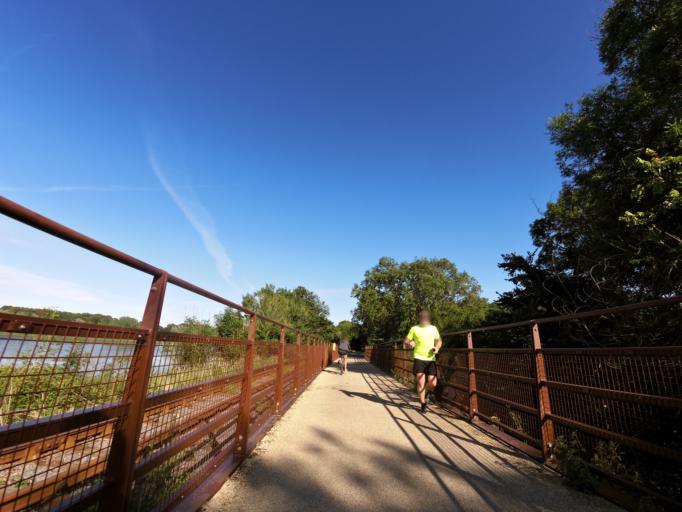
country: IE
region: Leinster
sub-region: Kilkenny
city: Mooncoin
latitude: 52.2462
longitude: -7.2304
